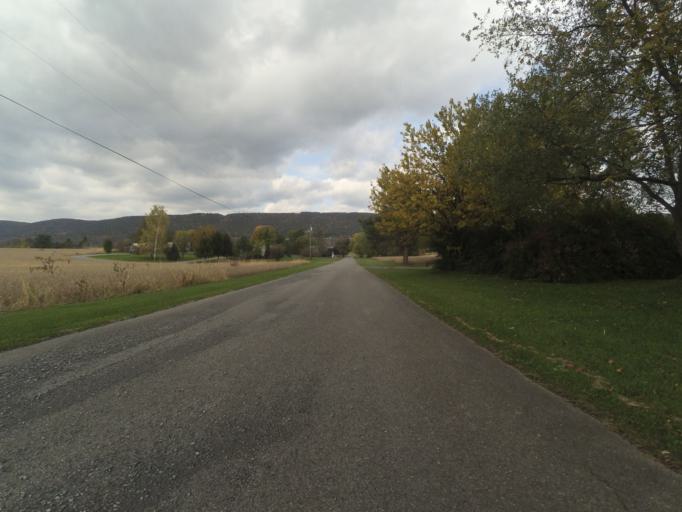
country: US
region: Pennsylvania
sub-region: Centre County
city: Bellefonte
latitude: 40.8895
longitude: -77.8142
